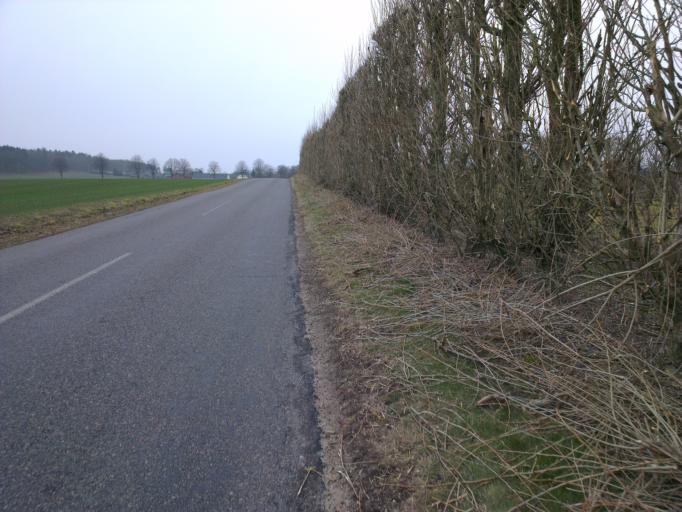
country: DK
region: Capital Region
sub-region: Frederikssund Kommune
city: Skibby
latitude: 55.7925
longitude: 11.9668
